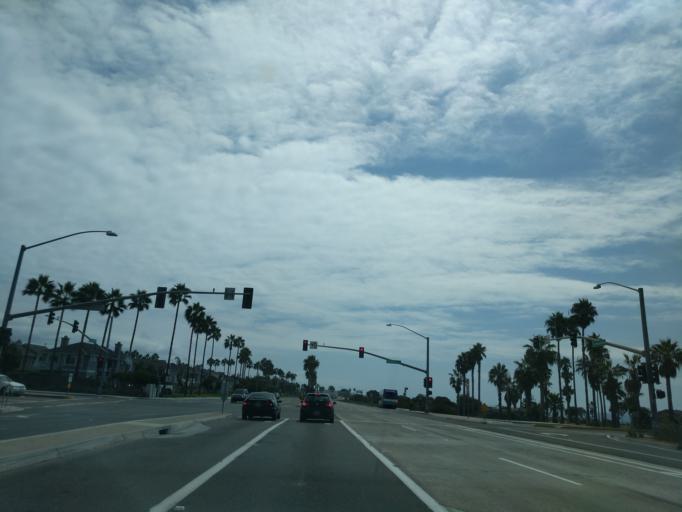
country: US
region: California
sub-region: San Diego County
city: Carlsbad
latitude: 33.1022
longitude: -117.3184
